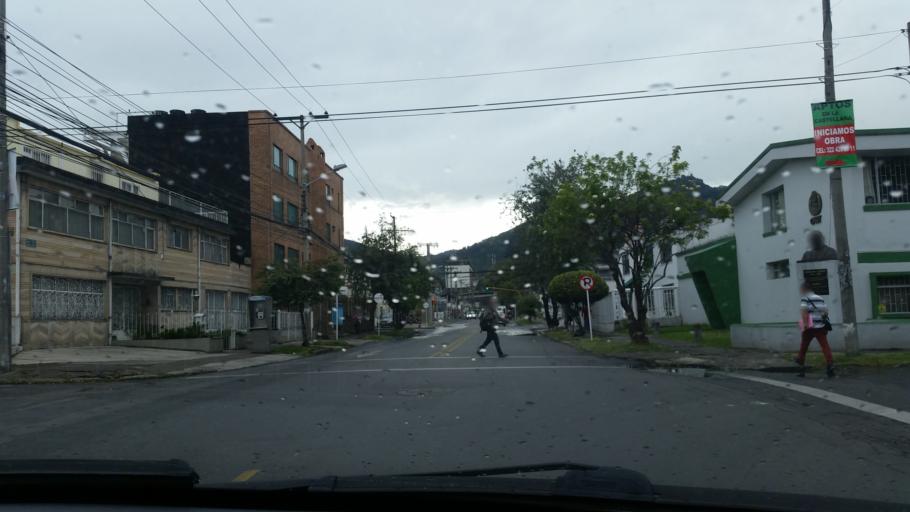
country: CO
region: Bogota D.C.
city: Barrio San Luis
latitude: 4.6808
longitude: -74.0615
